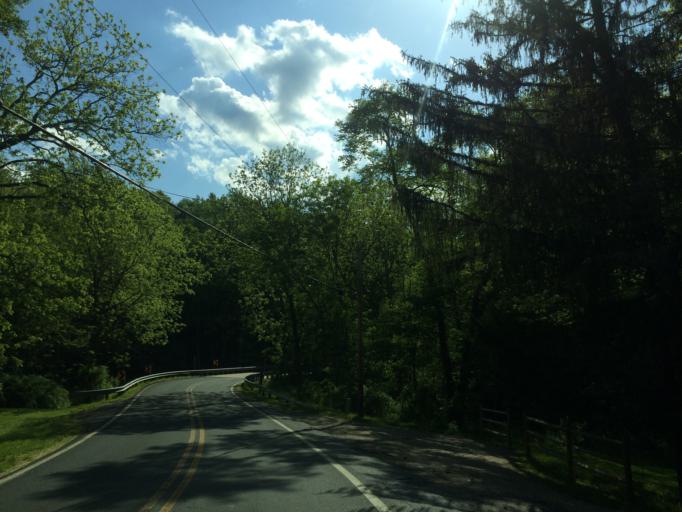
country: US
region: Maryland
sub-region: Carroll County
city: Eldersburg
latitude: 39.4665
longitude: -76.9700
